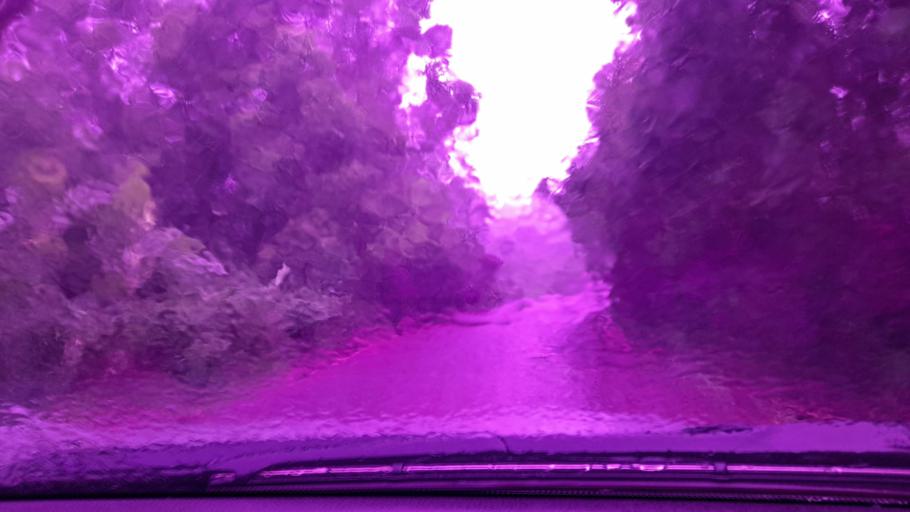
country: ET
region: Oromiya
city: Metu
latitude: 8.3603
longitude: 35.5932
